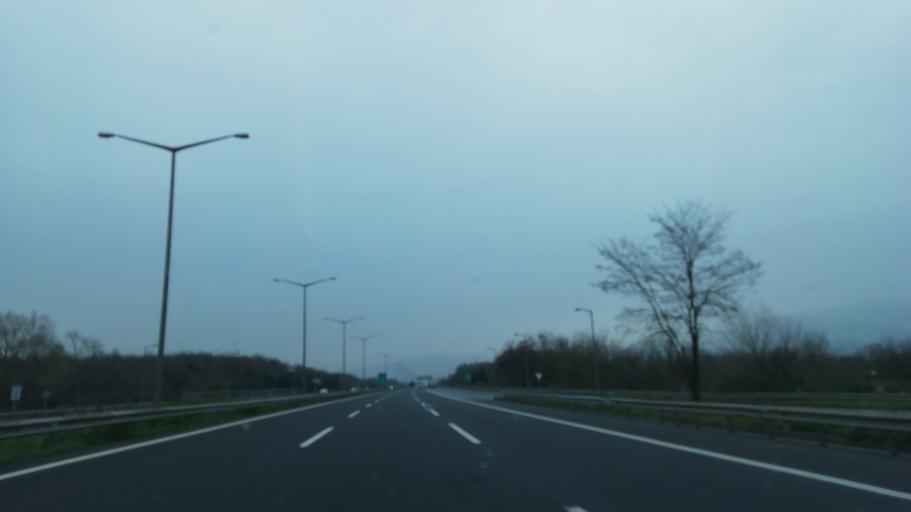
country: TR
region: Sakarya
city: Hendek
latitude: 40.7528
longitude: 30.7017
